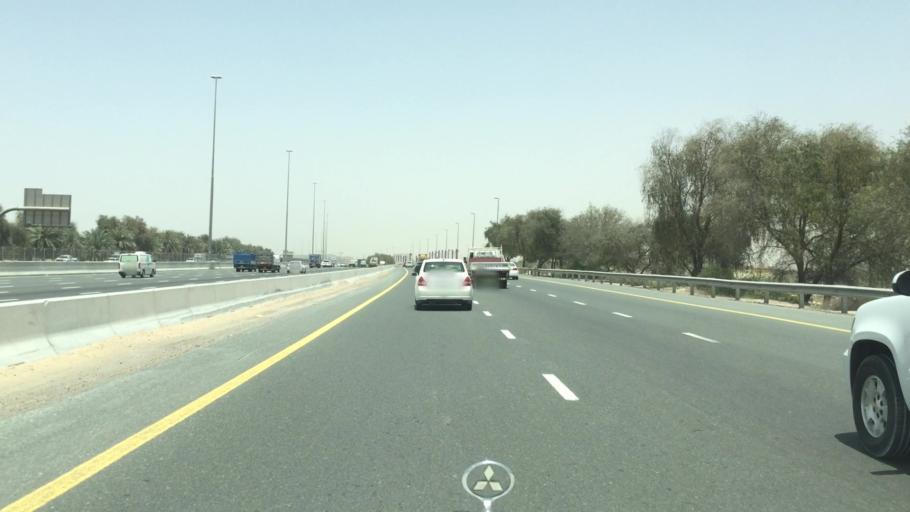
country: AE
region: Dubai
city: Dubai
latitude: 25.1237
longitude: 55.3706
